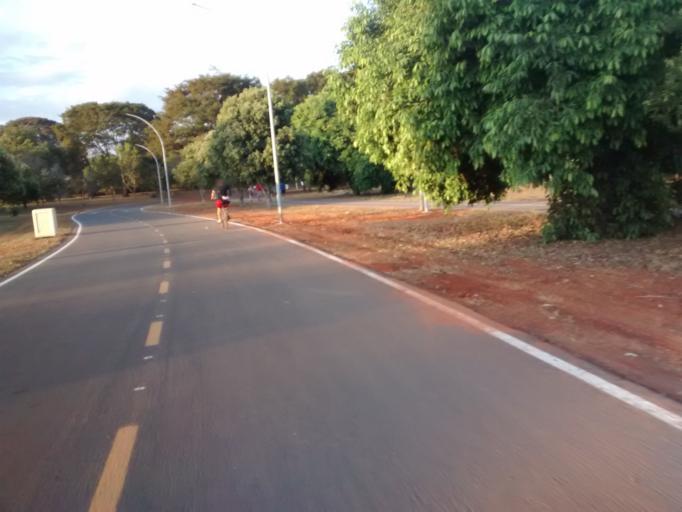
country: BR
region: Federal District
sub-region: Brasilia
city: Brasilia
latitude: -15.8038
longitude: -47.9109
